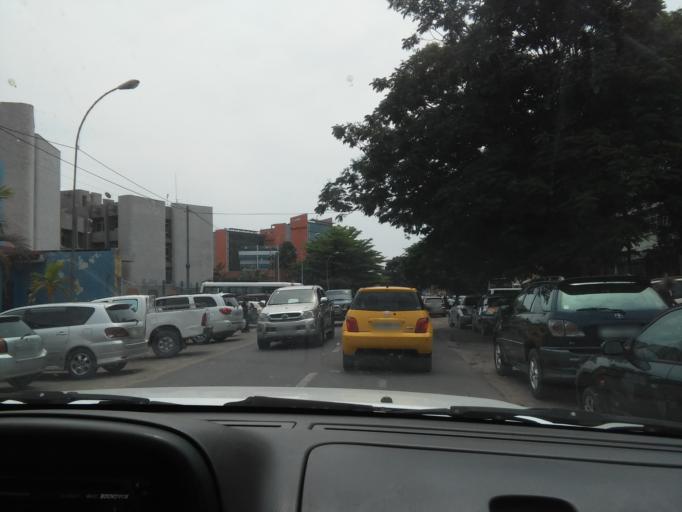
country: CD
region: Kinshasa
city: Kinshasa
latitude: -4.3063
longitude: 15.2932
